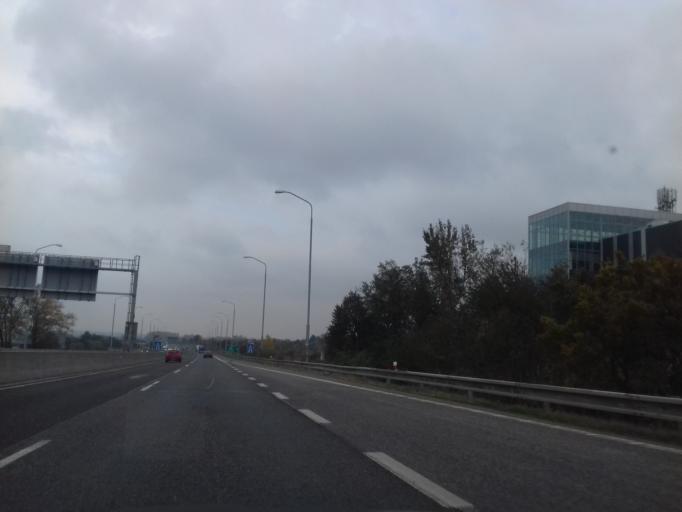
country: SK
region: Bratislavsky
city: Stupava
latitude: 48.2071
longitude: 17.0389
